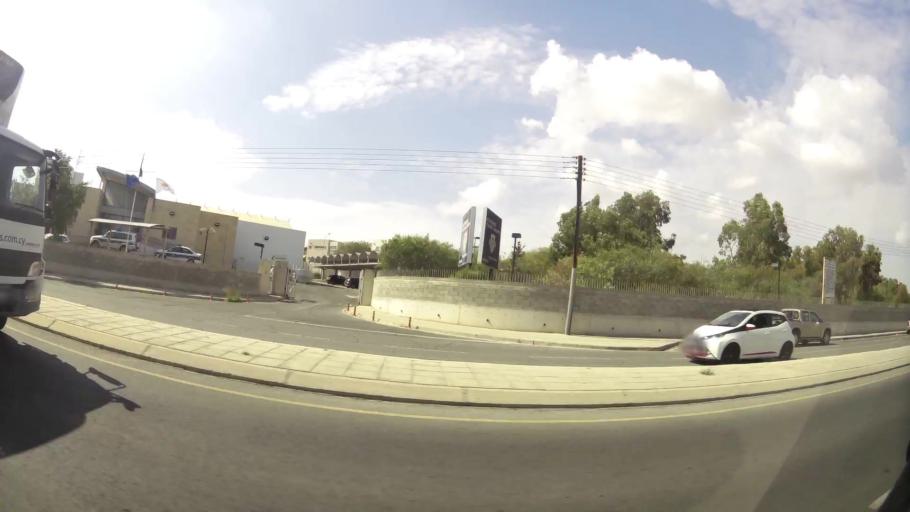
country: CY
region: Larnaka
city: Aradippou
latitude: 34.9448
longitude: 33.5797
